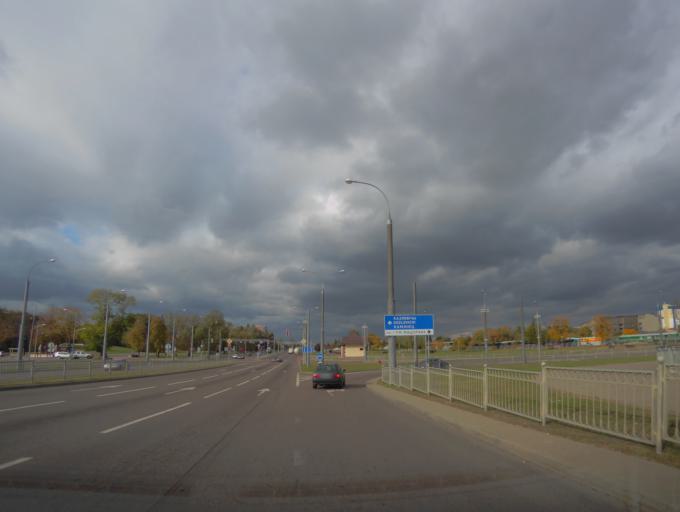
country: BY
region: Brest
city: Brest
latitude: 52.0847
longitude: 23.6700
